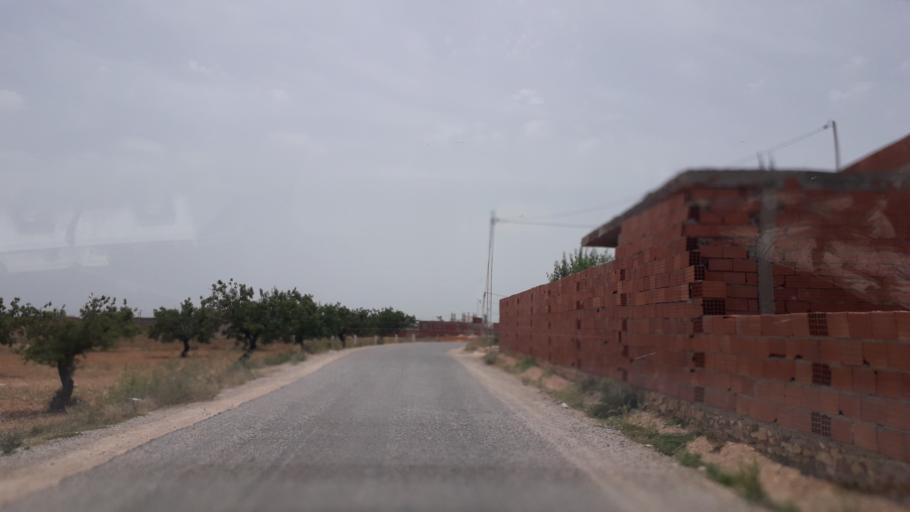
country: TN
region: Safaqis
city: Al Qarmadah
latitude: 34.8464
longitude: 10.7756
